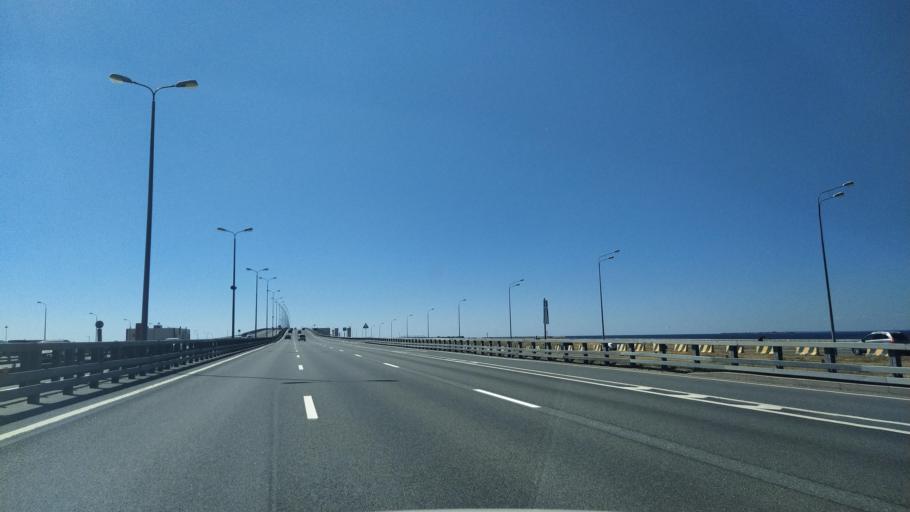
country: RU
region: St.-Petersburg
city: Kronshtadt
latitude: 60.0267
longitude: 29.8486
